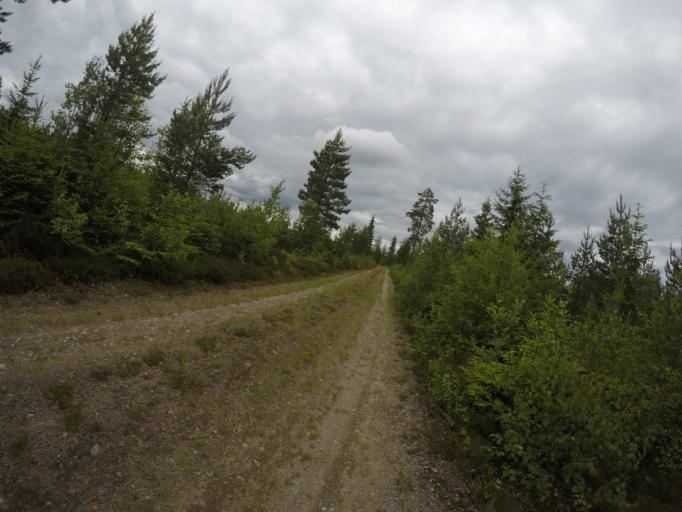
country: SE
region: OErebro
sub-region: Hallefors Kommun
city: Haellefors
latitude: 60.0590
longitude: 14.5262
